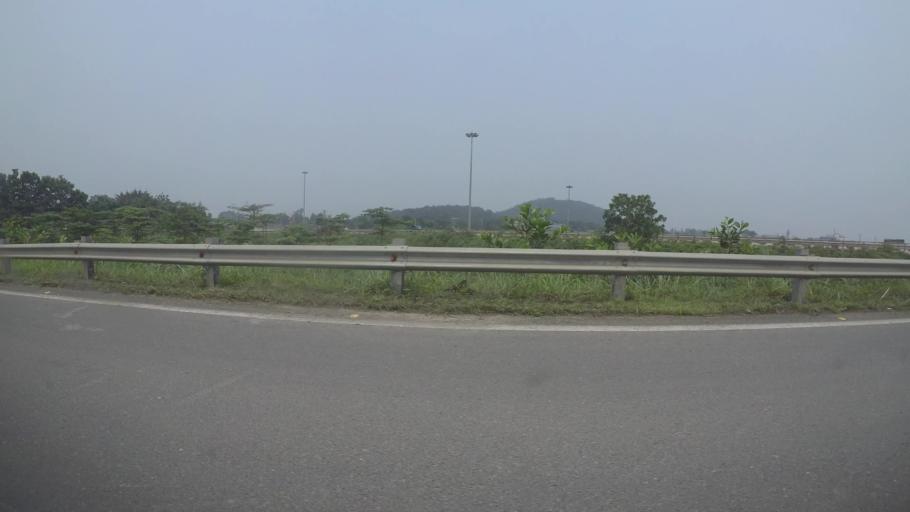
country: VN
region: Ha Noi
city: Lien Quan
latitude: 20.9897
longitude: 105.5232
